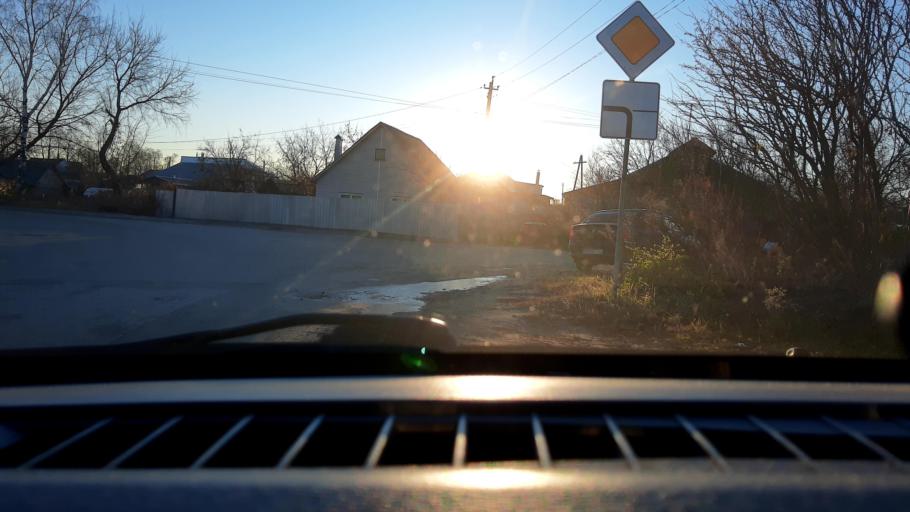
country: RU
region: Nizjnij Novgorod
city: Kstovo
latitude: 56.1805
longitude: 44.1701
